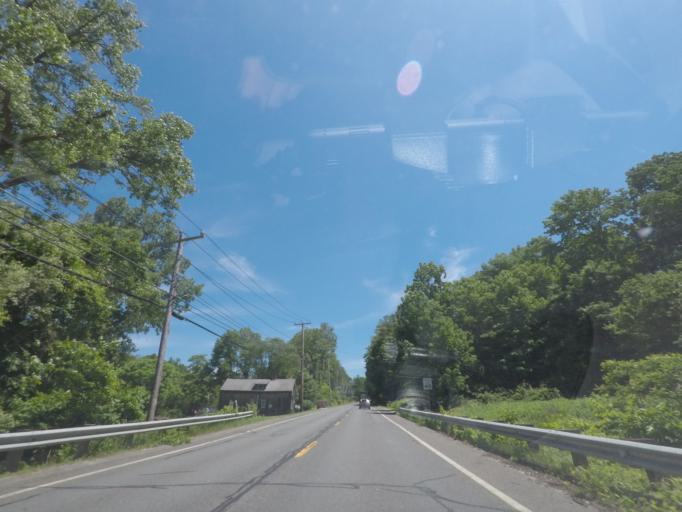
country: US
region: Massachusetts
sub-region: Berkshire County
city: Lee
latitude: 42.2997
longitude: -73.2139
